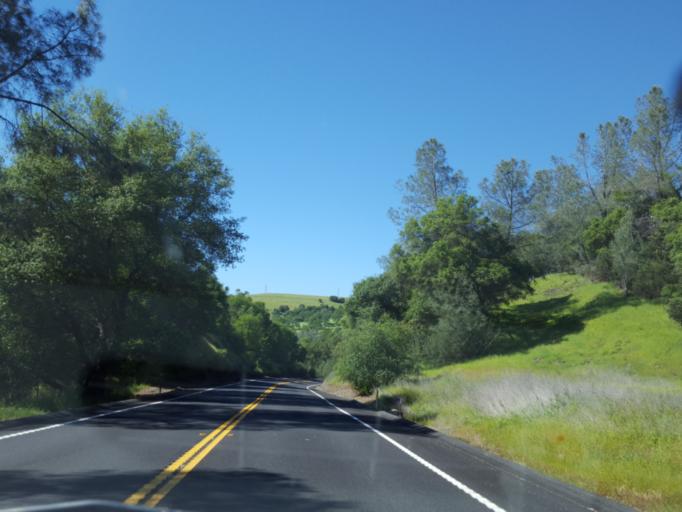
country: US
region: California
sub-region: Calaveras County
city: San Andreas
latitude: 38.2657
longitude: -120.7156
